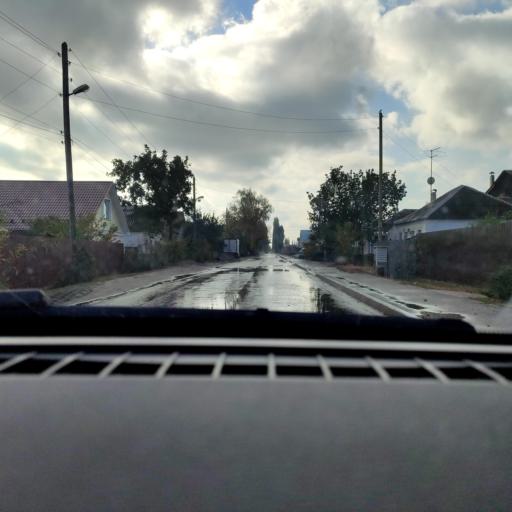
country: RU
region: Voronezj
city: Maslovka
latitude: 51.6081
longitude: 39.2207
